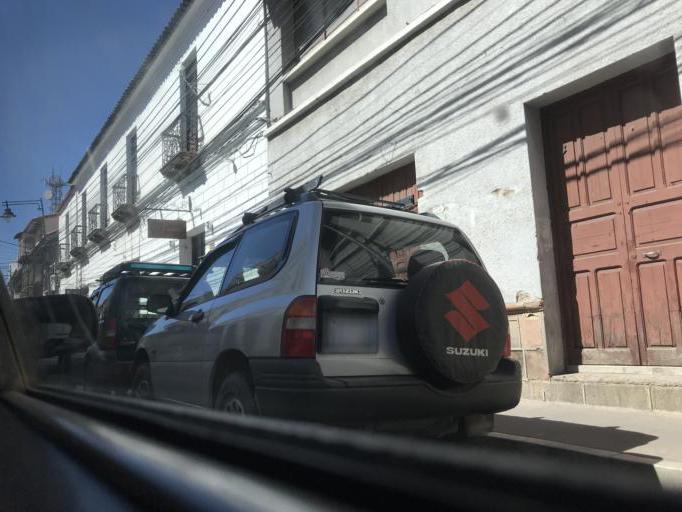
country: BO
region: Chuquisaca
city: Sucre
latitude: -19.0466
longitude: -65.2576
